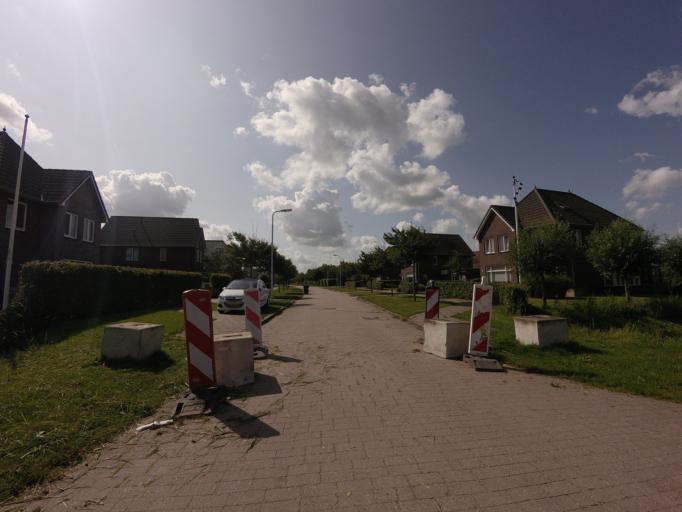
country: NL
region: Friesland
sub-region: Gemeente Het Bildt
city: Sint Annaparochie
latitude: 53.2818
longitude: 5.6588
